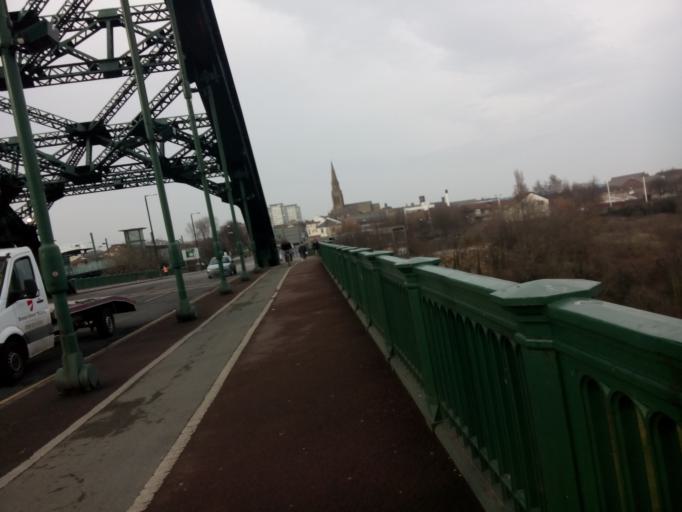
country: GB
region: England
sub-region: Sunderland
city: Sunderland
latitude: 54.9098
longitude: -1.3828
